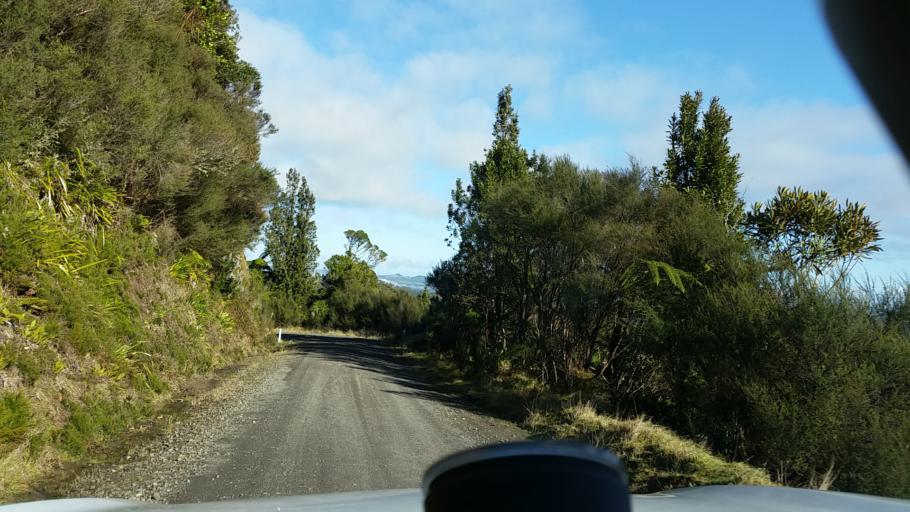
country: NZ
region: Taranaki
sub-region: South Taranaki District
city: Eltham
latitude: -39.4031
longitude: 174.5620
